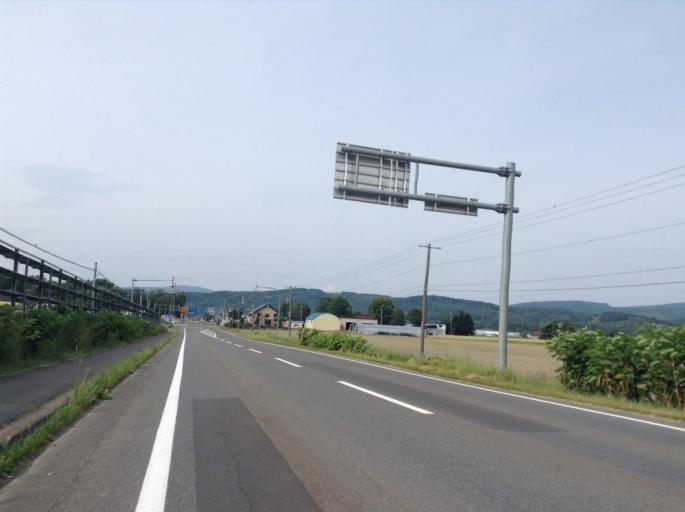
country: JP
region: Hokkaido
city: Nayoro
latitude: 44.4343
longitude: 142.4023
